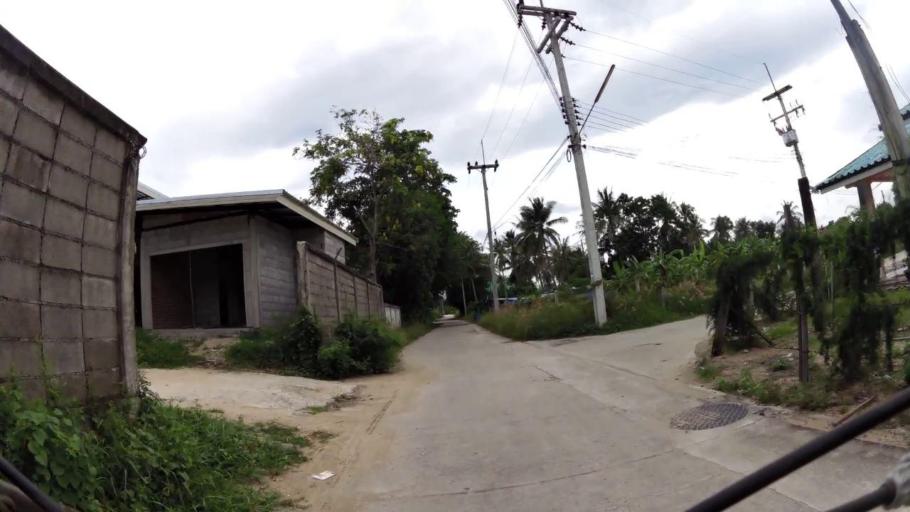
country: TH
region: Prachuap Khiri Khan
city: Prachuap Khiri Khan
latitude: 11.7370
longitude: 99.7779
